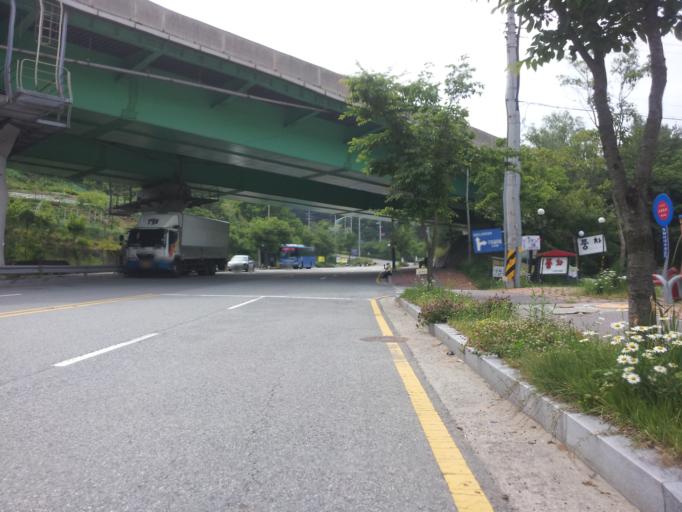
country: KR
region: Daejeon
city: Daejeon
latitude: 36.3323
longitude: 127.4800
